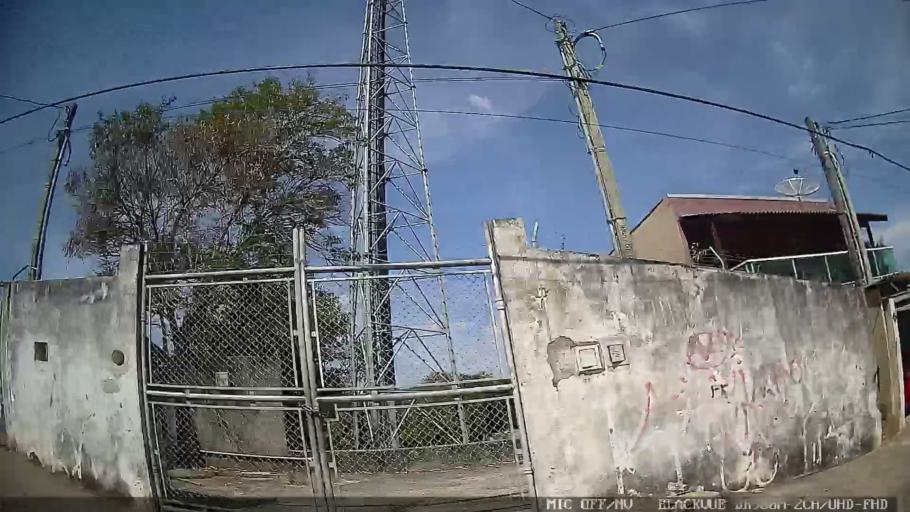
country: BR
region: Sao Paulo
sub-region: Cabreuva
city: Cabreuva
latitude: -23.2573
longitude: -47.0553
